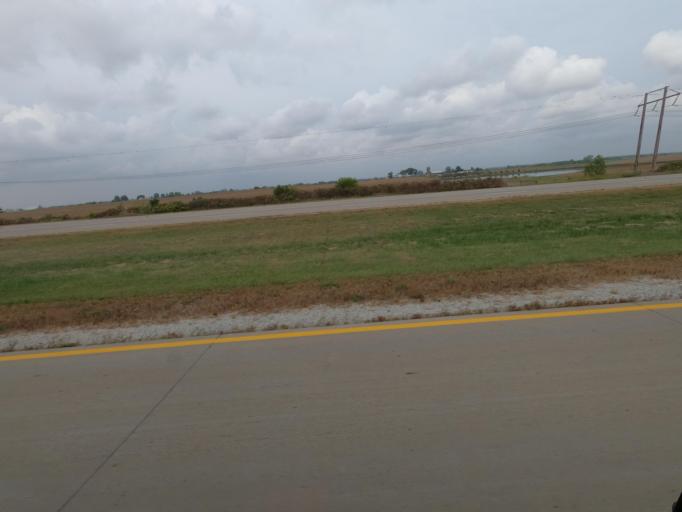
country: US
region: Iowa
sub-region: Wapello County
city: Ottumwa
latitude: 41.0900
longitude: -92.4039
